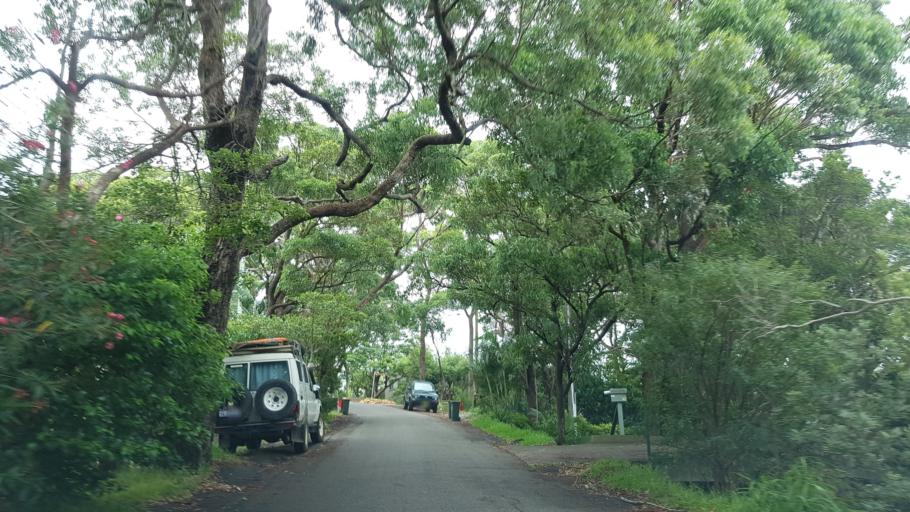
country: AU
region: New South Wales
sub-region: Pittwater
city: North Narrabeen
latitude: -33.7067
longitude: 151.2868
